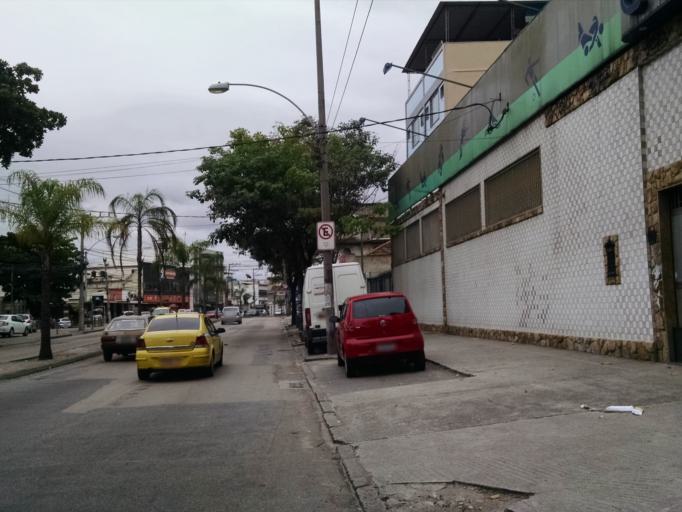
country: BR
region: Rio de Janeiro
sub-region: Duque De Caxias
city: Duque de Caxias
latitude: -22.8412
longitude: -43.3166
